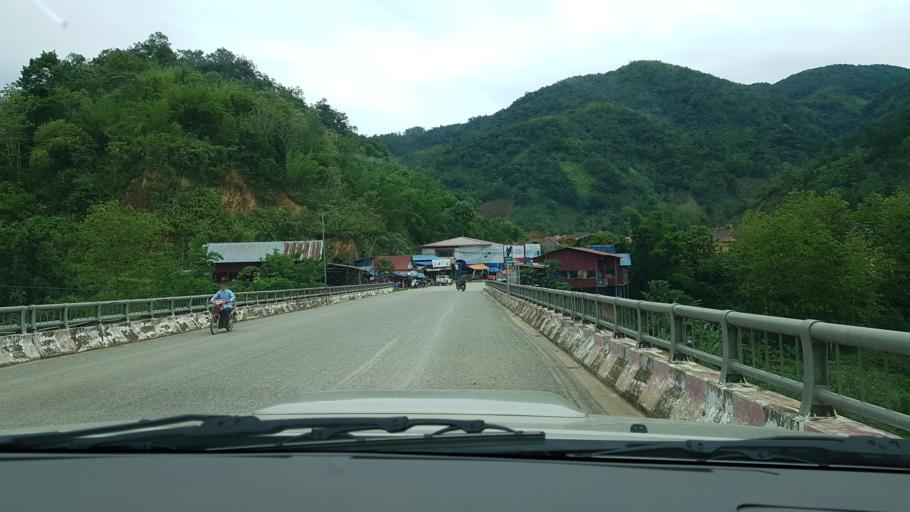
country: LA
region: Phongsali
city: Khoa
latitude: 21.0803
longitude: 102.5069
